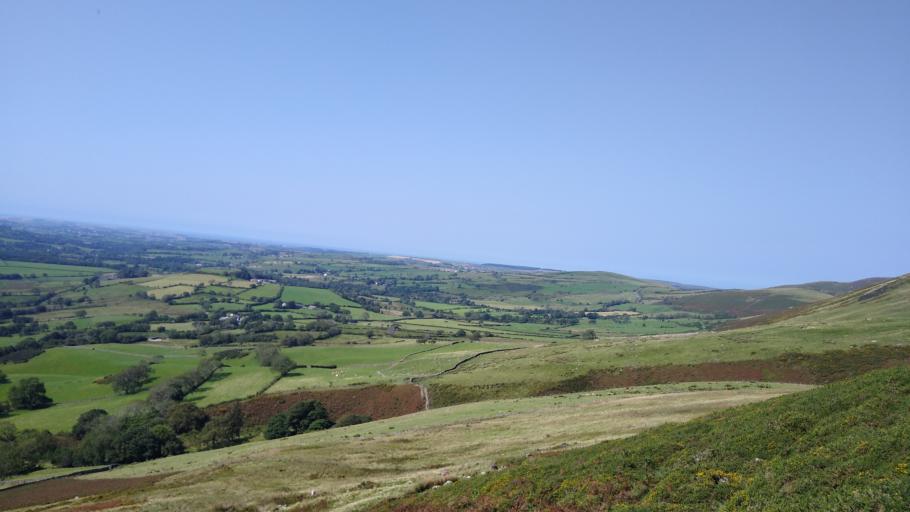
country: GB
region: England
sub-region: Cumbria
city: Frizington
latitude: 54.5370
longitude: -3.3766
